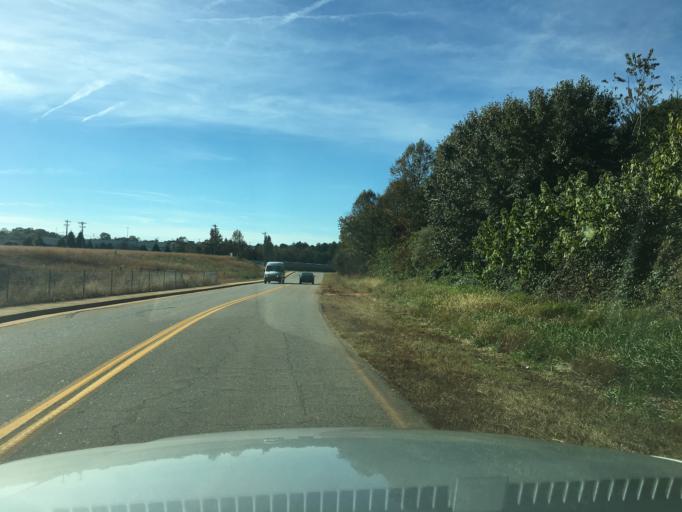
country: US
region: North Carolina
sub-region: Catawba County
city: Saint Stephens
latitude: 35.7041
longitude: -81.2819
